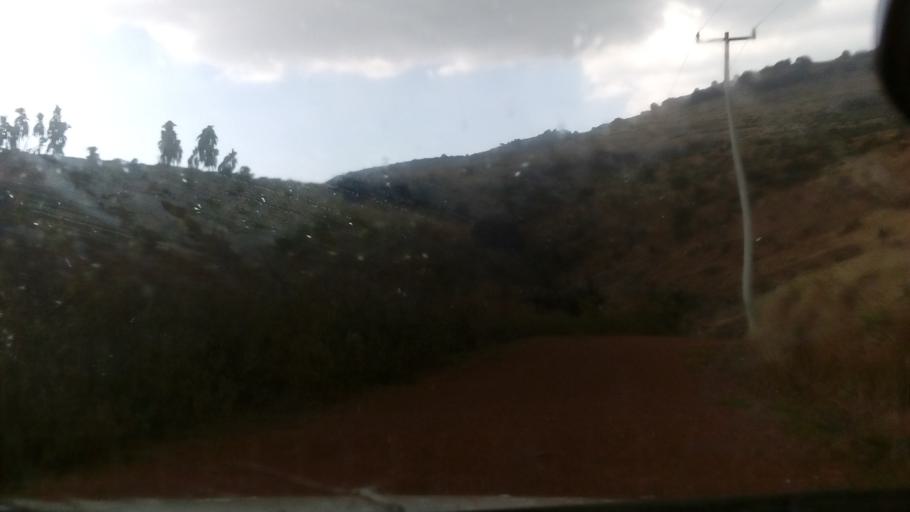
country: MX
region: Guanajuato
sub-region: Silao de la Victoria
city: San Francisco (Banos de Agua Caliente)
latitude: 21.1505
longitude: -101.4353
